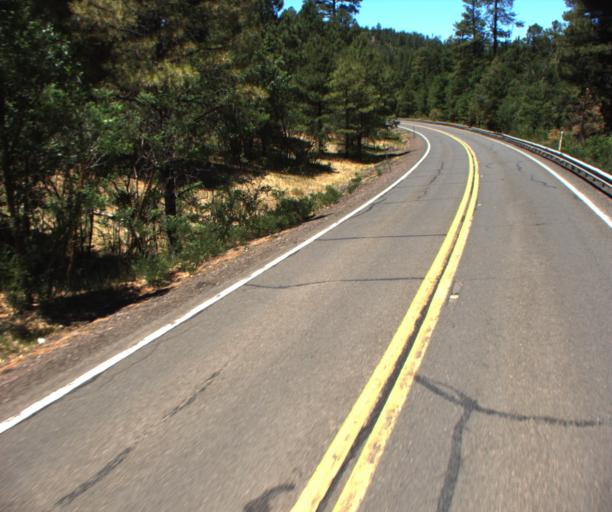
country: US
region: Arizona
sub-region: Gila County
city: Pine
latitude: 34.6064
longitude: -111.2280
